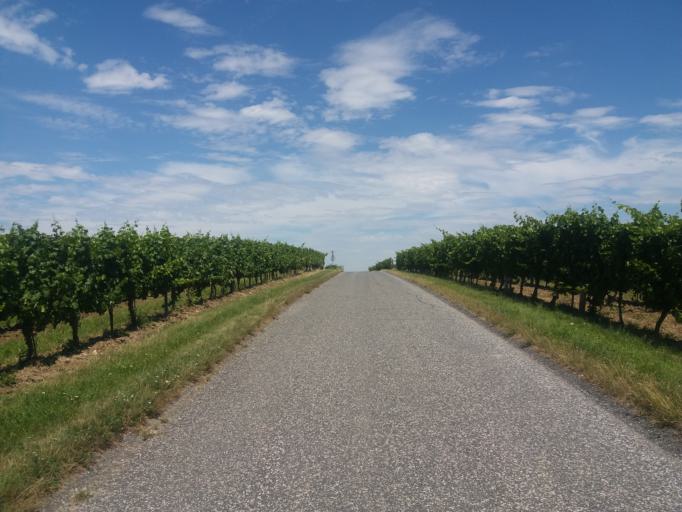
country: AT
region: Burgenland
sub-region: Politischer Bezirk Oberpullendorf
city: Raiding
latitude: 47.5702
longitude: 16.5398
